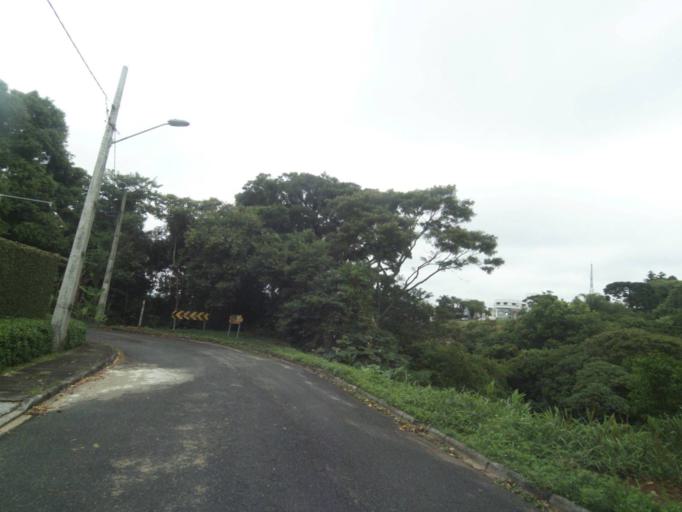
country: BR
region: Parana
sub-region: Curitiba
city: Curitiba
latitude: -25.4128
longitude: -49.2893
